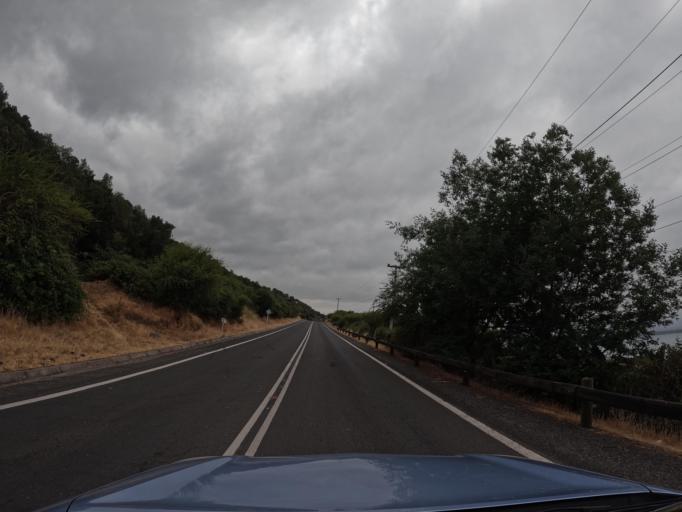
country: CL
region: O'Higgins
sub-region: Provincia de Colchagua
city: Chimbarongo
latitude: -34.7374
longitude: -71.1165
